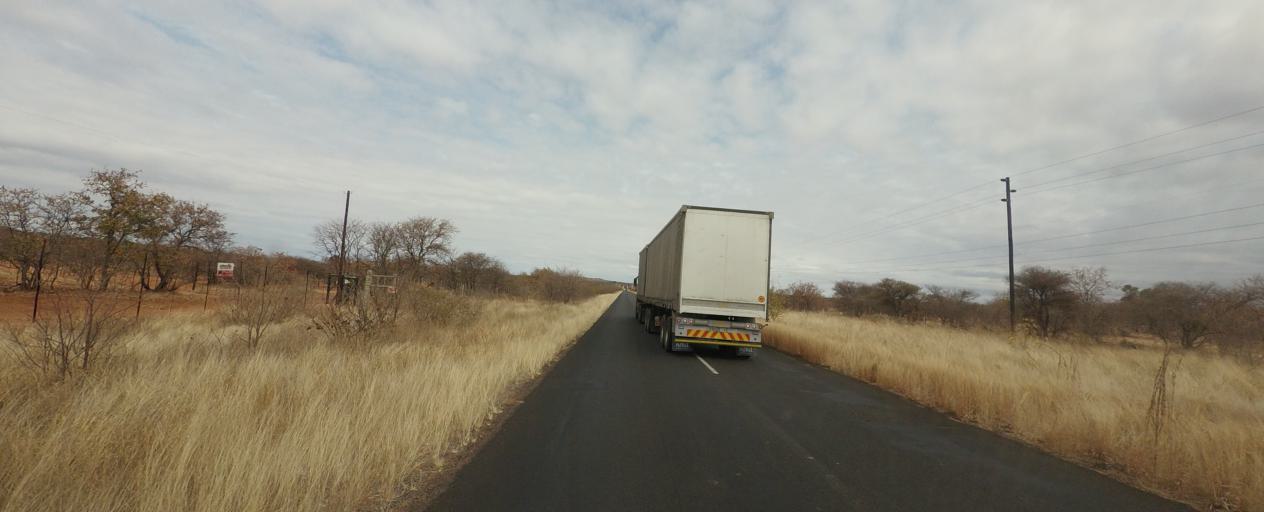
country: ZW
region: Matabeleland South
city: Beitbridge
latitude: -22.4302
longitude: 29.4390
